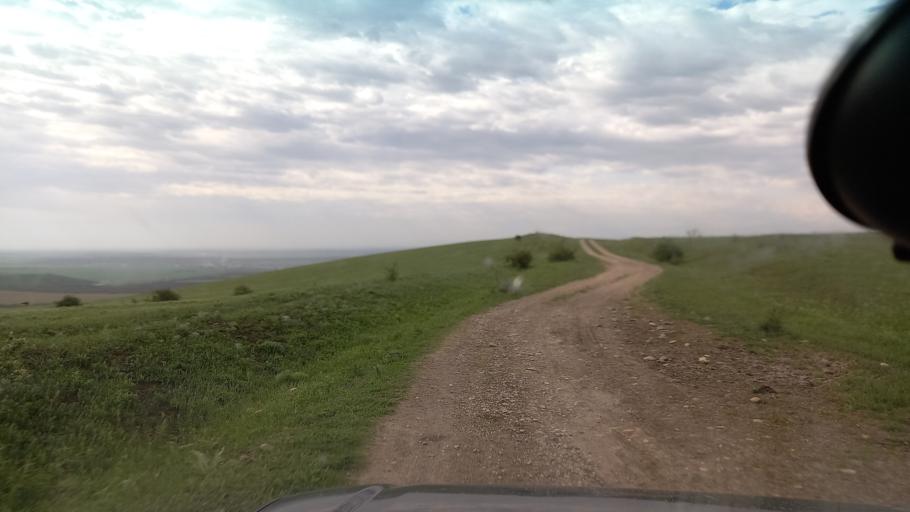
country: RU
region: Kabardino-Balkariya
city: Kuba-Taba
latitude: 43.8079
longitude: 43.4076
